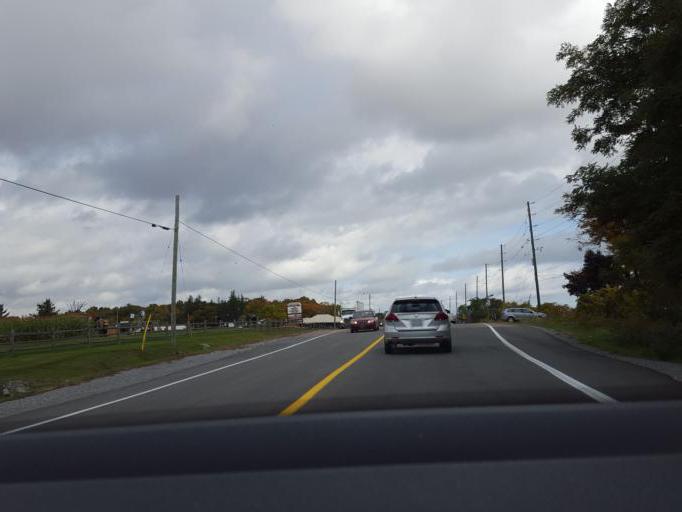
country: CA
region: Ontario
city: Pickering
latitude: 43.8523
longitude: -79.1834
